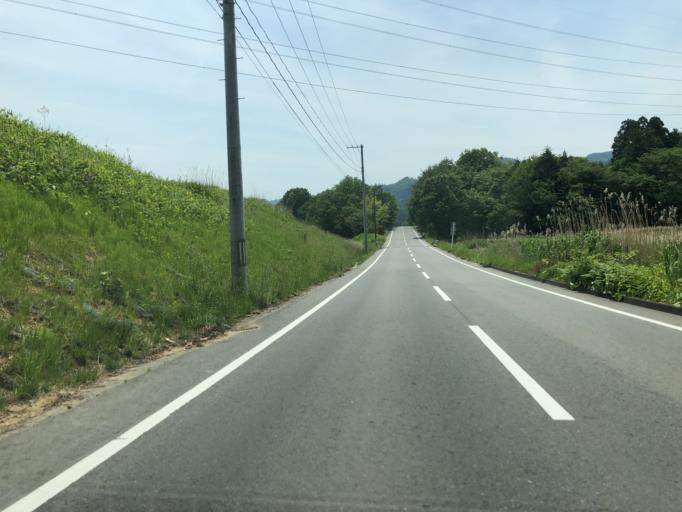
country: JP
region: Fukushima
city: Namie
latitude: 37.5282
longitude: 140.9363
